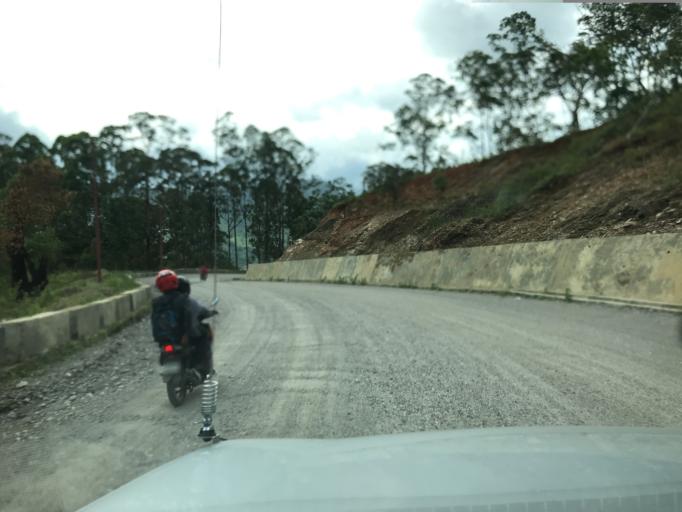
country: TL
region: Aileu
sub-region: Aileu Villa
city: Aileu
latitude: -8.6637
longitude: 125.5359
